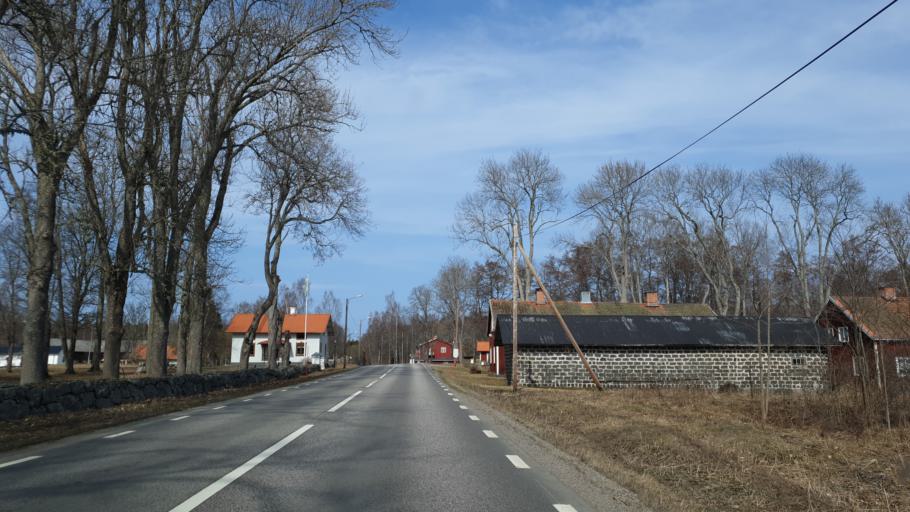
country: SE
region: Gaevleborg
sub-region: Gavle Kommun
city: Norrsundet
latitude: 61.0457
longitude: 17.1447
